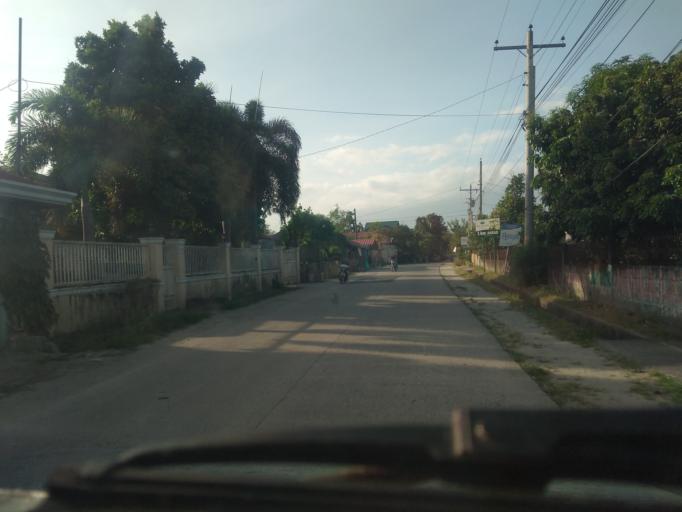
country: PH
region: Central Luzon
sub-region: Province of Pampanga
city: Bulaon
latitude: 15.0950
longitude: 120.6829
